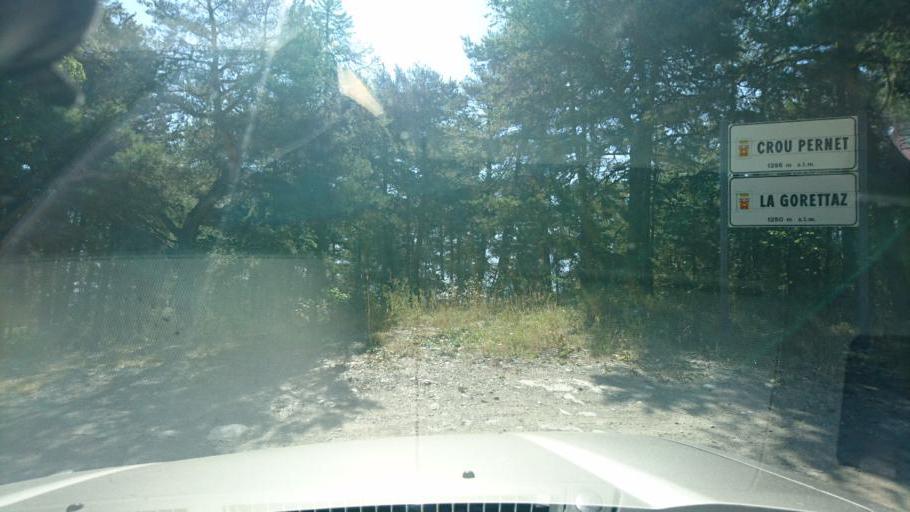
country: IT
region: Aosta Valley
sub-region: Valle d'Aosta
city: Ville Sur Sarre
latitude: 45.7335
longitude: 7.2430
